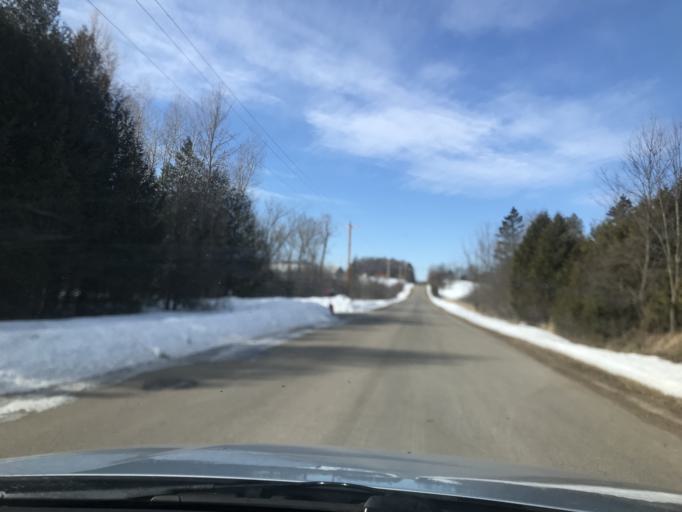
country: US
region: Wisconsin
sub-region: Oconto County
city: Gillett
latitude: 44.9618
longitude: -88.2943
